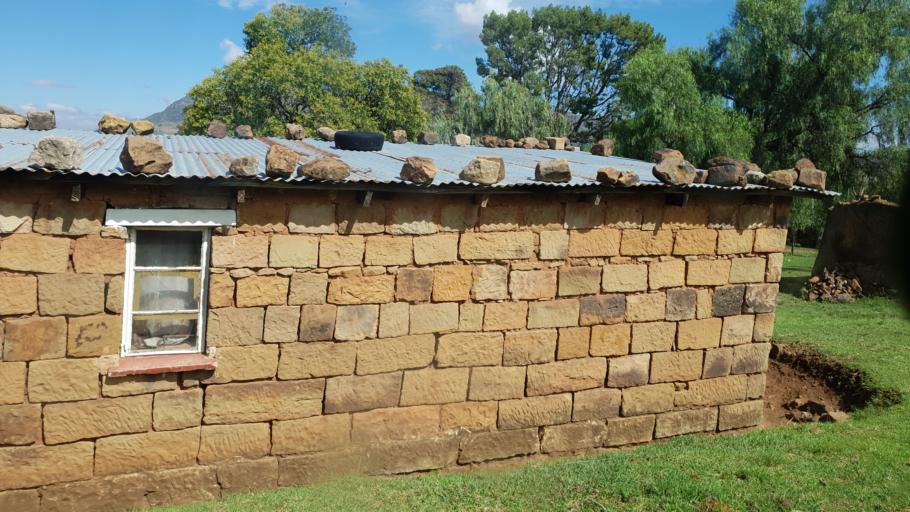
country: LS
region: Maseru
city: Nako
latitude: -29.6252
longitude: 27.5125
